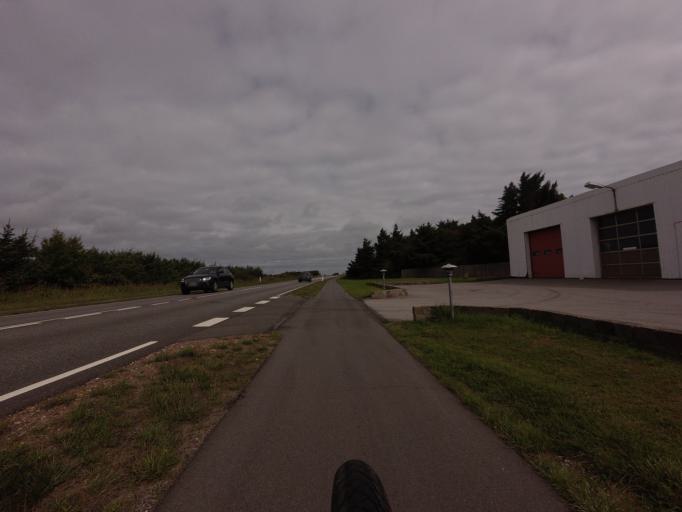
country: DK
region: North Denmark
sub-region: Hjorring Kommune
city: Hirtshals
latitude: 57.5772
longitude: 9.9447
